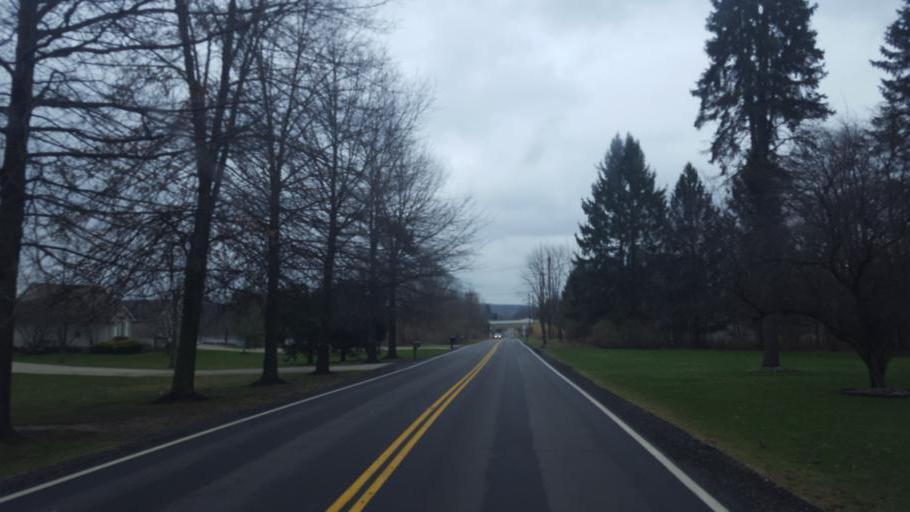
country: US
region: Ohio
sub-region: Medina County
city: Medina
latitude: 41.1066
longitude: -81.8205
